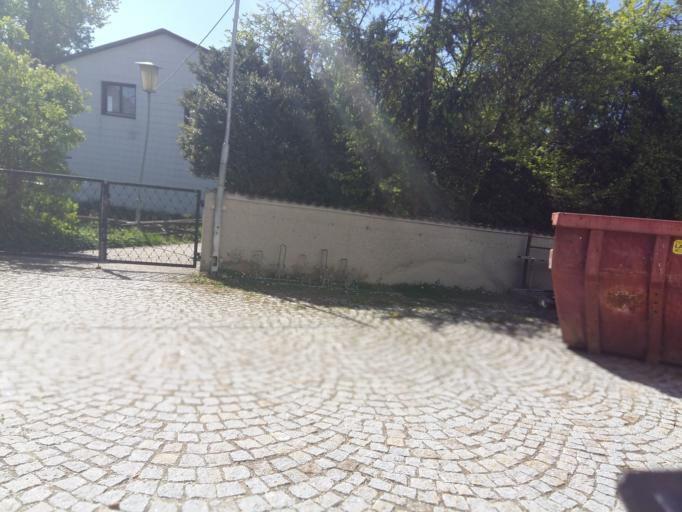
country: AT
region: Upper Austria
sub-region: Politischer Bezirk Scharding
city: Sankt Marienkirchen bei Schaerding
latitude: 48.3885
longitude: 13.4509
